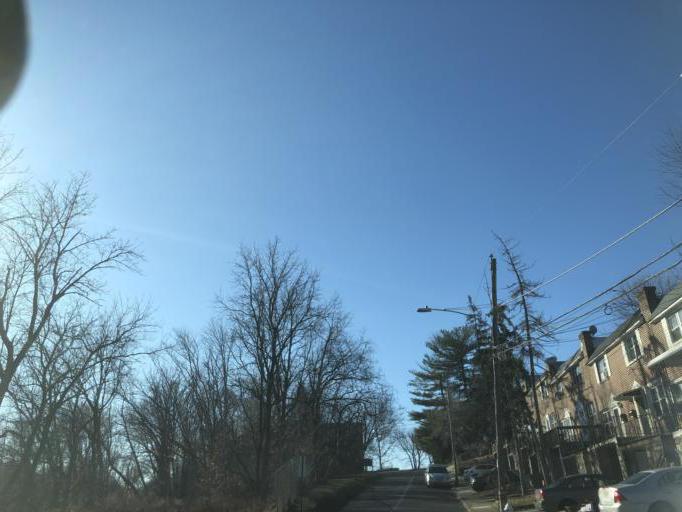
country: US
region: Pennsylvania
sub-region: Delaware County
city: Millbourne
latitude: 39.9532
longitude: -75.2522
